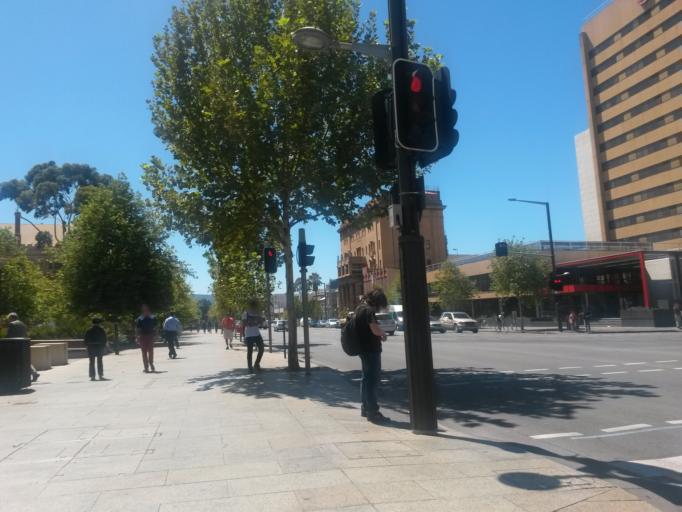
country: AU
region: South Australia
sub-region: Adelaide
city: Adelaide
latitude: -34.9213
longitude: 138.6053
